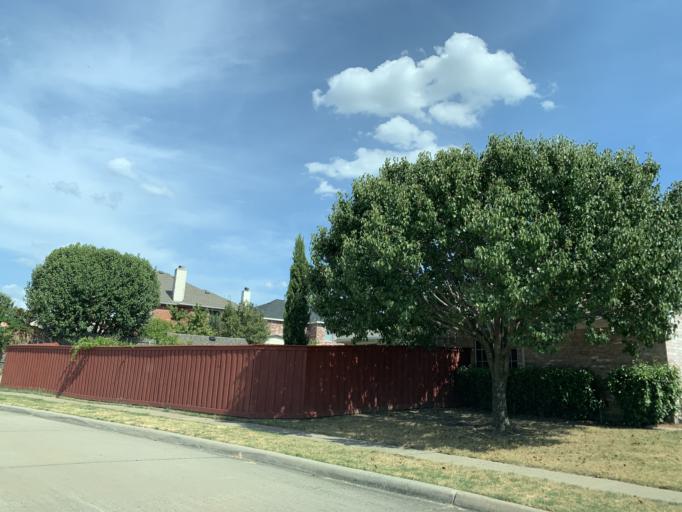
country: US
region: Texas
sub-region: Dallas County
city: Cedar Hill
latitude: 32.6493
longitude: -97.0082
